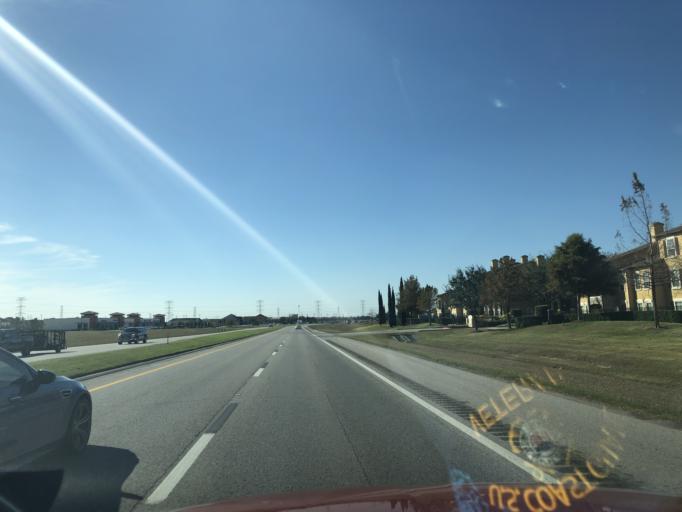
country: US
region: Texas
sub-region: Galveston County
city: Dickinson
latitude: 29.4975
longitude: -95.0579
